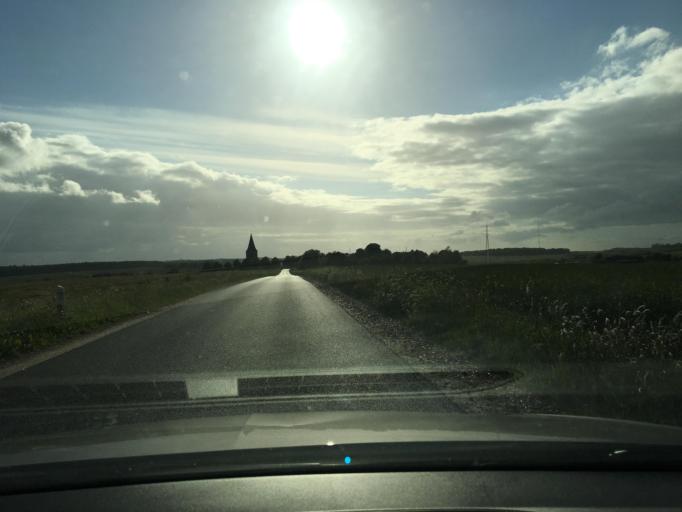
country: DK
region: Central Jutland
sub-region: Favrskov Kommune
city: Hinnerup
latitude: 56.2793
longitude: 10.0505
